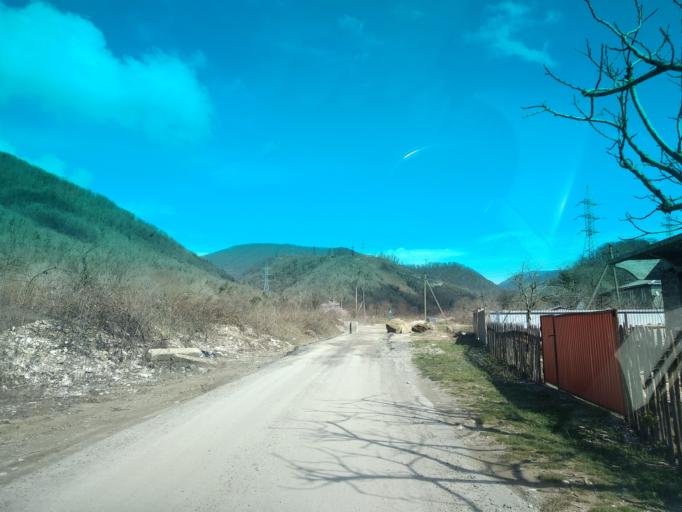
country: RU
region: Krasnodarskiy
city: Shepsi
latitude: 44.0564
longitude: 39.1653
